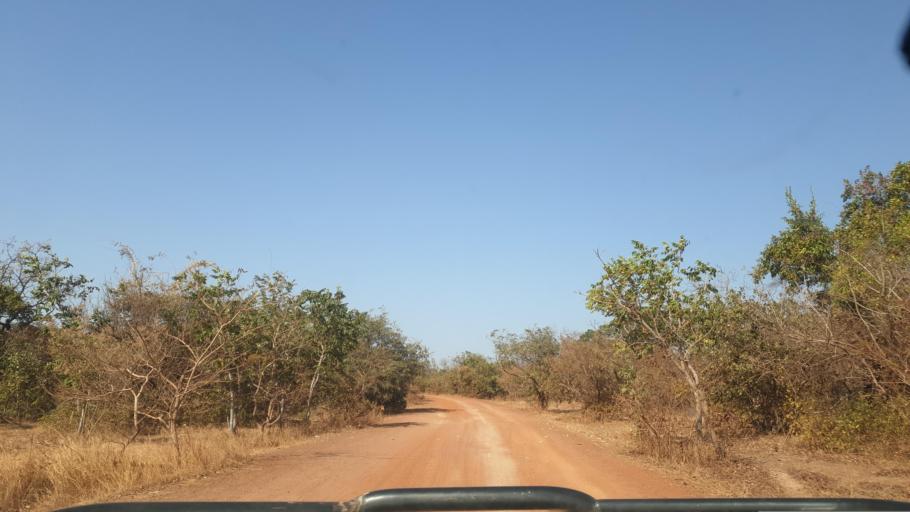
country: ML
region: Sikasso
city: Bougouni
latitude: 11.8205
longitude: -6.9511
